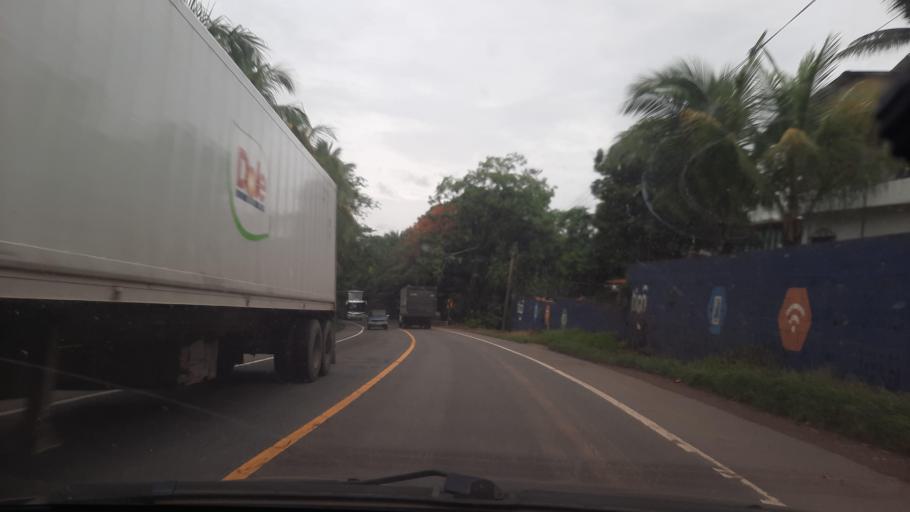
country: GT
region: Izabal
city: Morales
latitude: 15.4620
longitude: -88.9298
